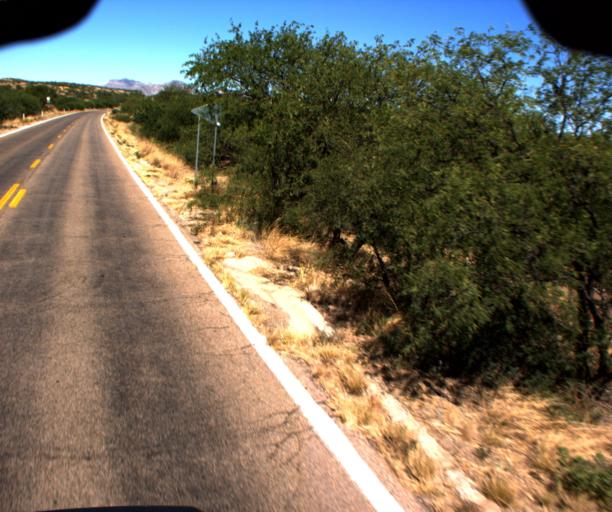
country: US
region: Arizona
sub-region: Santa Cruz County
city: Rio Rico
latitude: 31.4299
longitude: -110.9754
